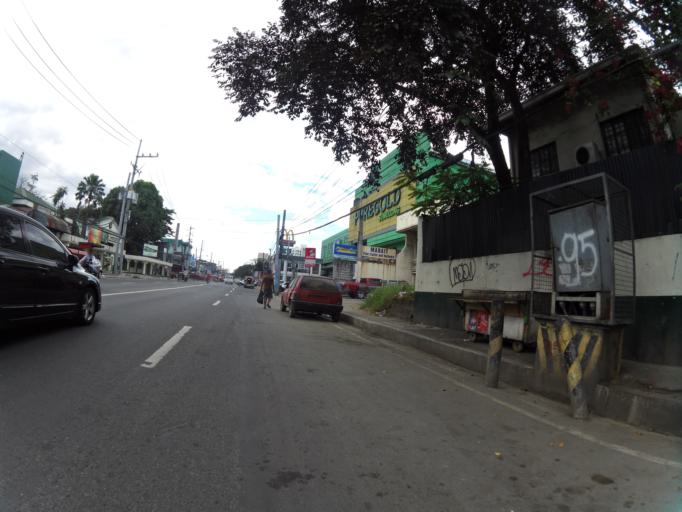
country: PH
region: Calabarzon
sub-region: Province of Rizal
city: Antipolo
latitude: 14.6334
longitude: 121.1096
